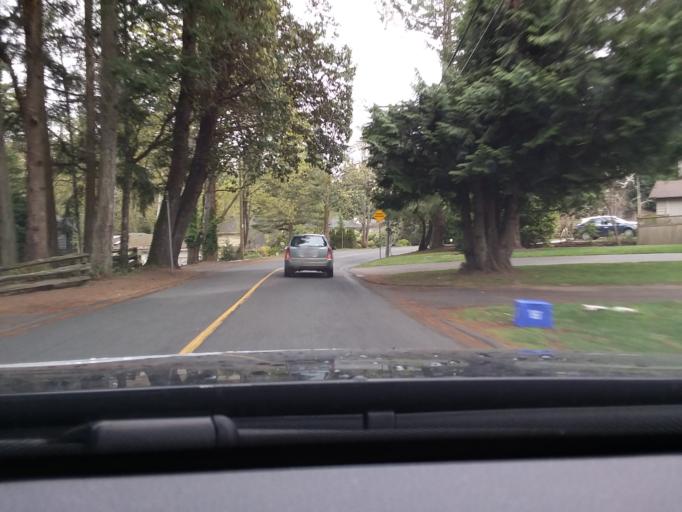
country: CA
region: British Columbia
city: Victoria
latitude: 48.5216
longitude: -123.3786
